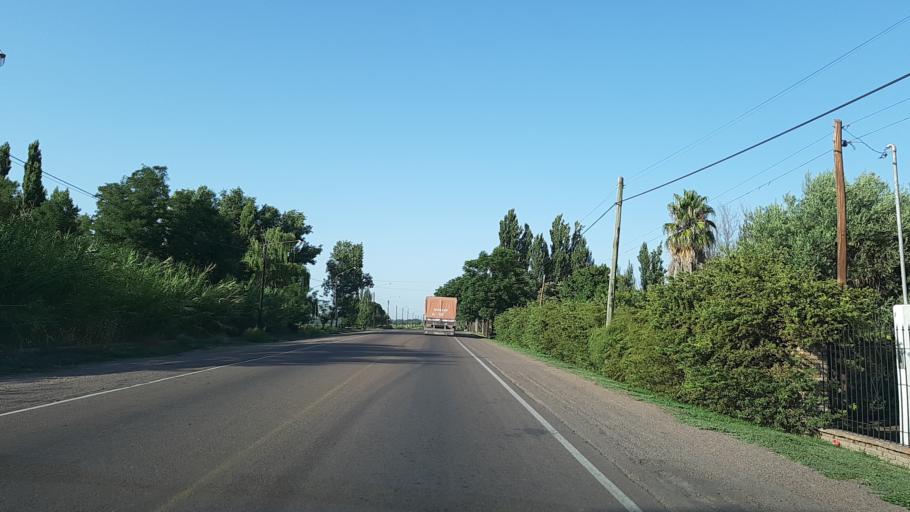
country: AR
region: Mendoza
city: San Martin
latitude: -32.9873
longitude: -68.4662
